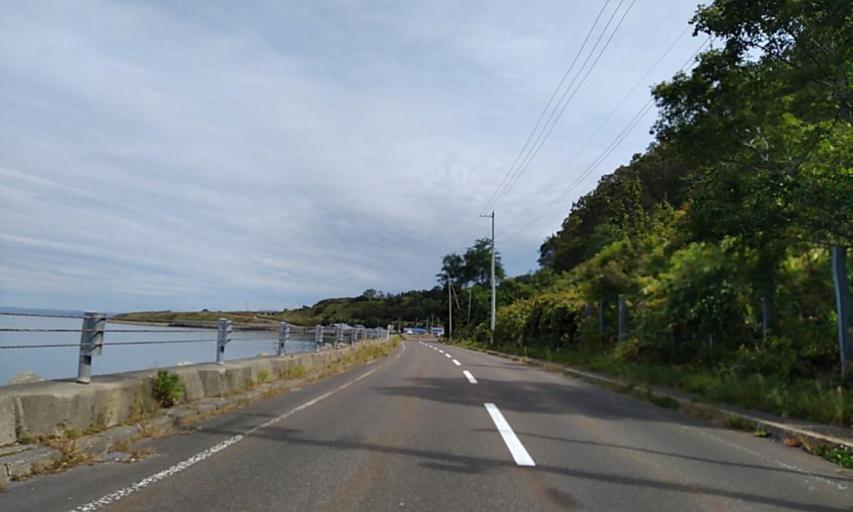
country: JP
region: Hokkaido
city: Rumoi
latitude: 43.8521
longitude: 141.5386
